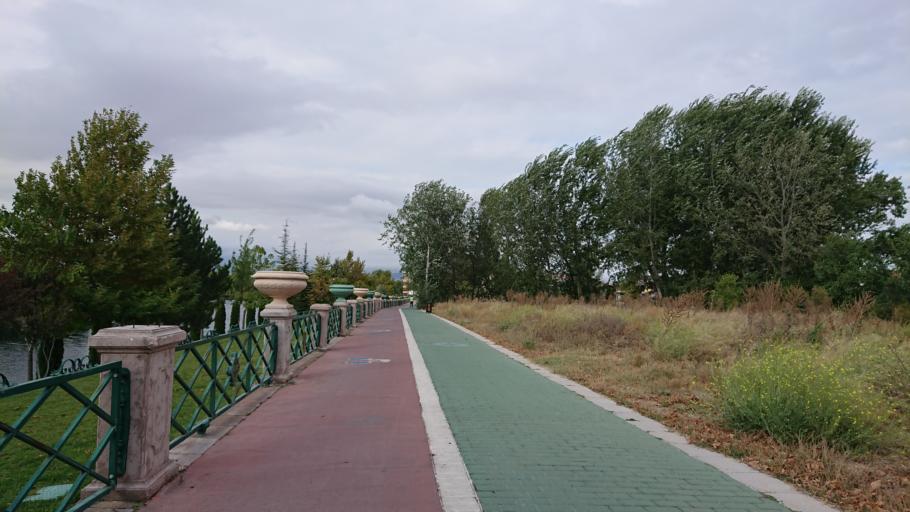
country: TR
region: Eskisehir
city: Eskisehir
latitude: 39.7611
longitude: 30.4854
